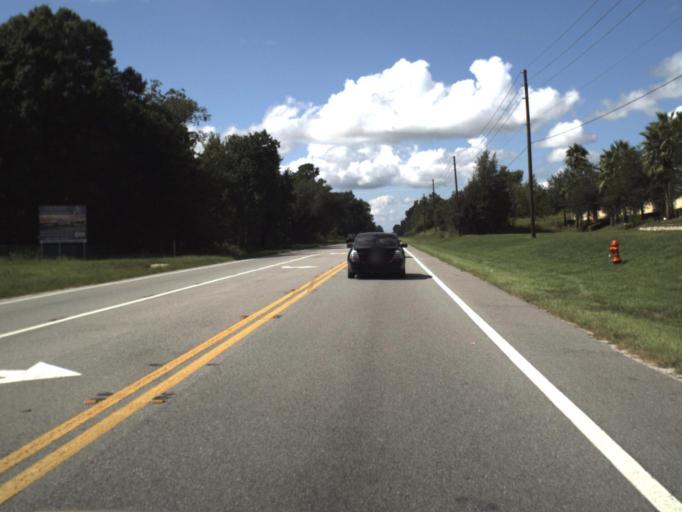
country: US
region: Florida
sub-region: Polk County
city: Loughman
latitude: 28.2316
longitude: -81.5624
